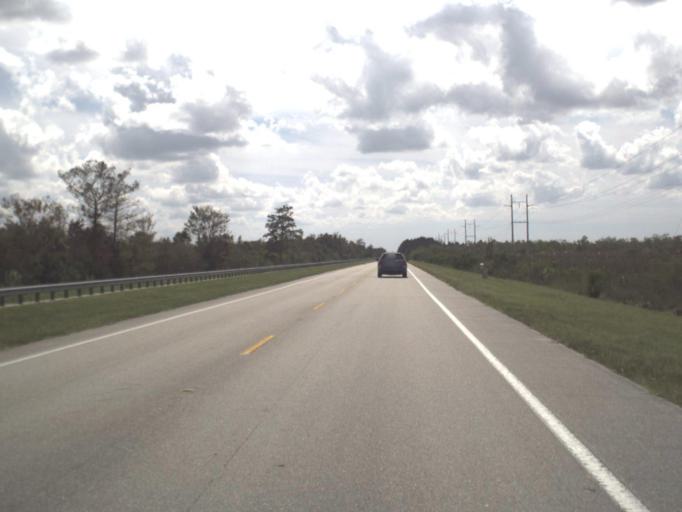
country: US
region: Florida
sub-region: Collier County
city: Lely Resort
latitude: 26.0164
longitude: -81.3459
